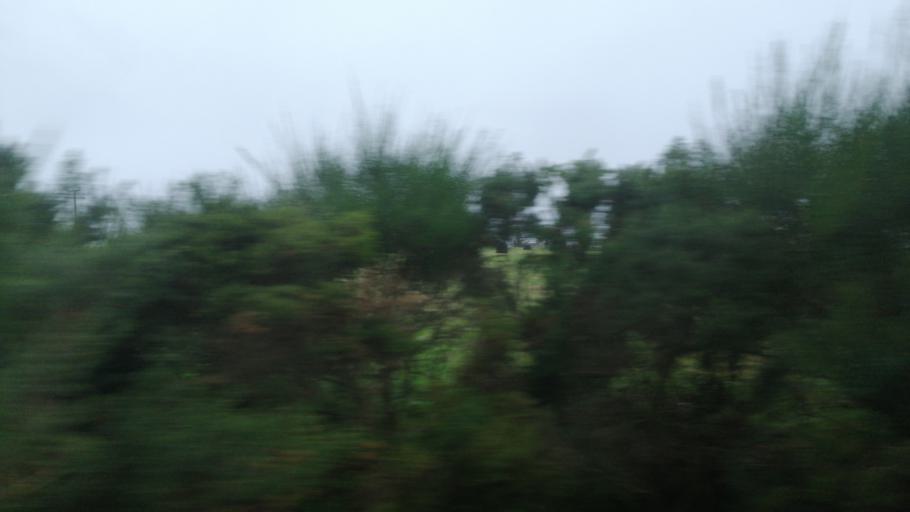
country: GB
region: Scotland
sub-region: Highland
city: Brora
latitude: 58.0279
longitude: -3.8505
